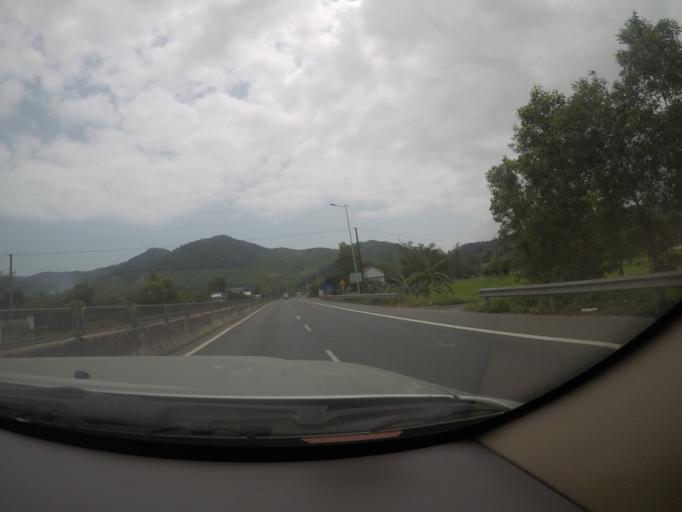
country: VN
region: Thua Thien-Hue
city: Phu Loc
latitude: 16.2699
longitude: 108.0258
